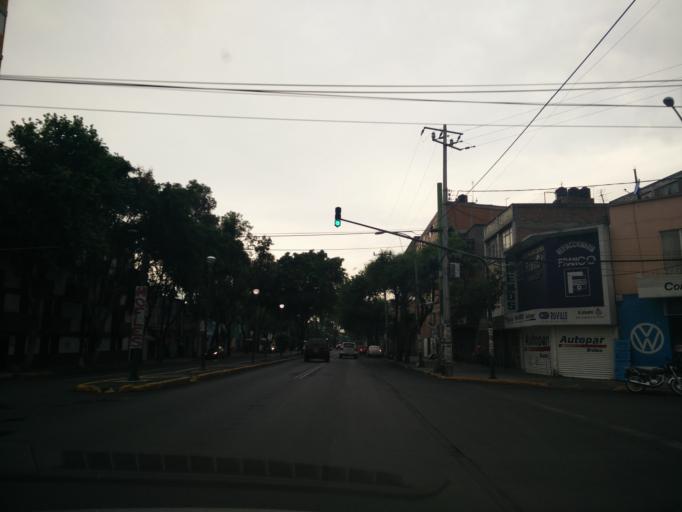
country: MX
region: Mexico City
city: Benito Juarez
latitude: 19.4113
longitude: -99.1490
